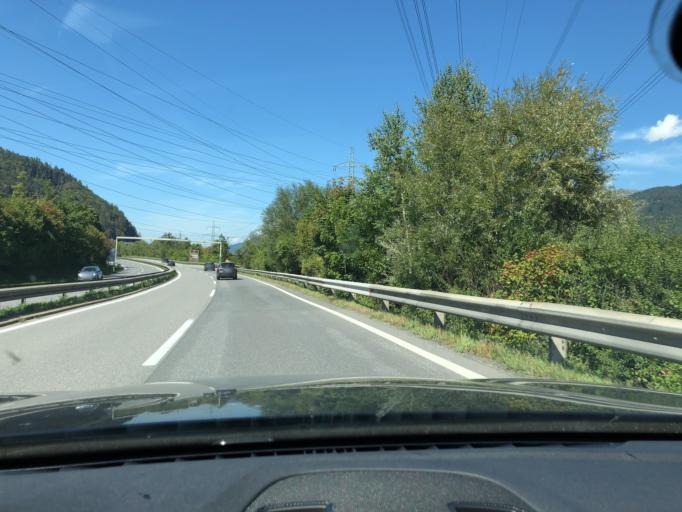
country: AT
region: Vorarlberg
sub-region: Politischer Bezirk Bludenz
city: Buers
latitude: 47.1574
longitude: 9.8060
